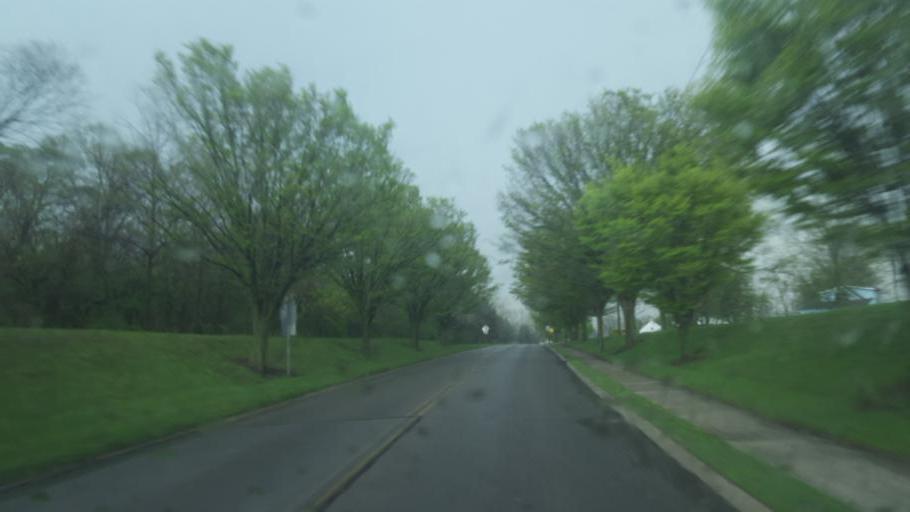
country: US
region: Ohio
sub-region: Seneca County
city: Fostoria
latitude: 41.1496
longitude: -83.4048
